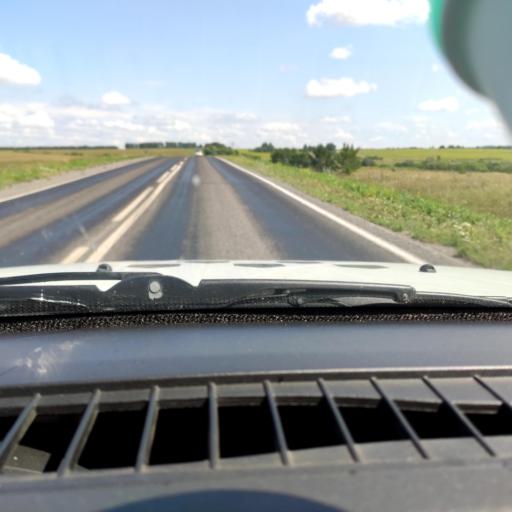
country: RU
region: Bashkortostan
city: Verkhniye Kigi
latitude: 55.4586
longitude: 58.4268
